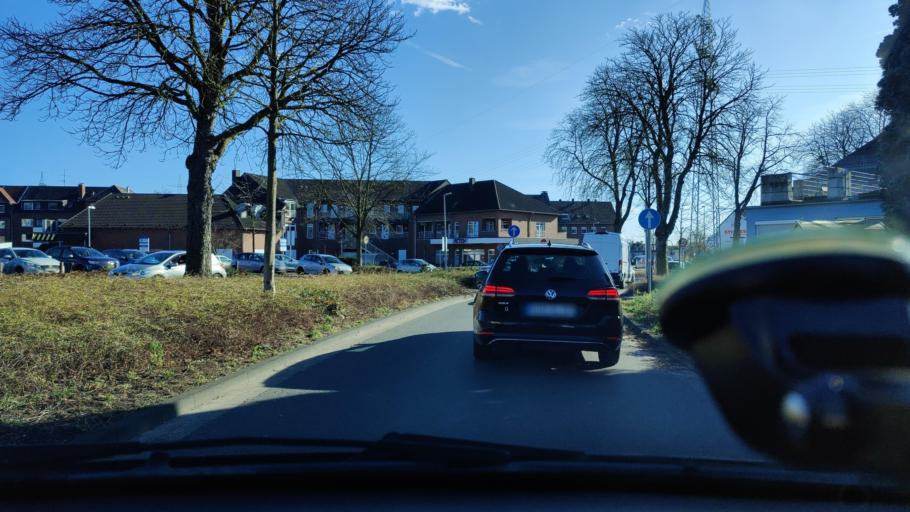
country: DE
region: North Rhine-Westphalia
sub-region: Regierungsbezirk Dusseldorf
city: Dinslaken
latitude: 51.5711
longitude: 6.7493
